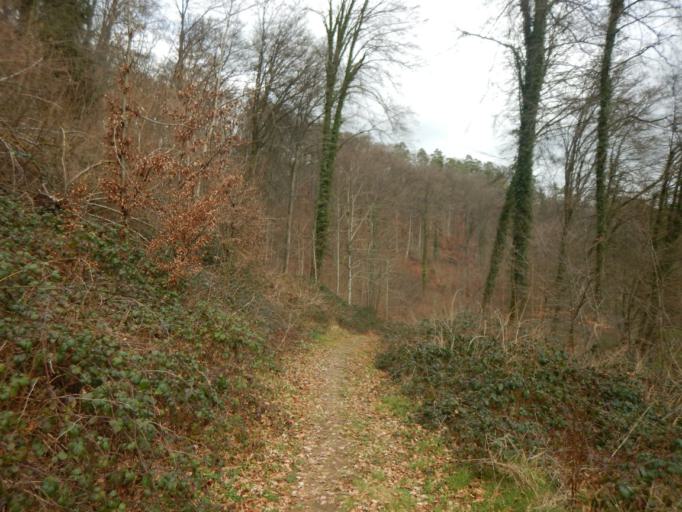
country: LU
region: Luxembourg
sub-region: Canton de Mersch
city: Tuntange
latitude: 49.7148
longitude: 6.0547
